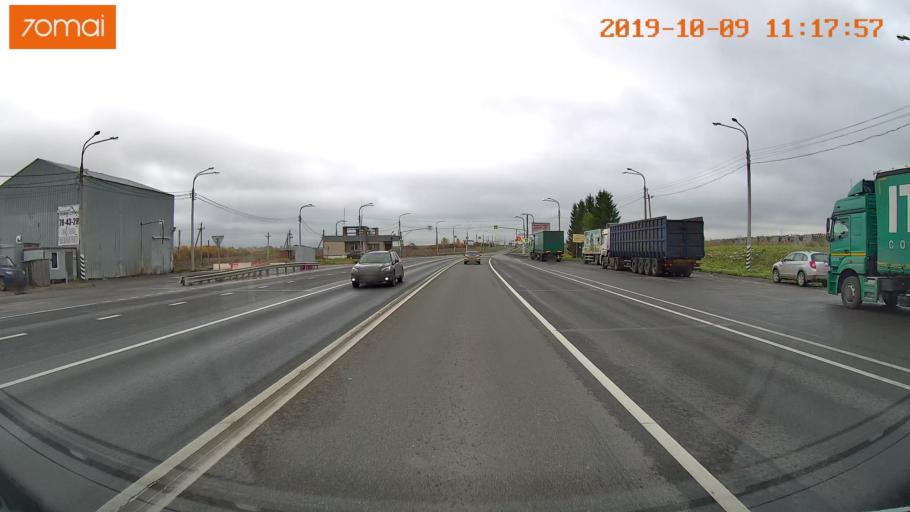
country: RU
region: Vologda
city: Vologda
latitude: 59.1714
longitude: 39.9075
